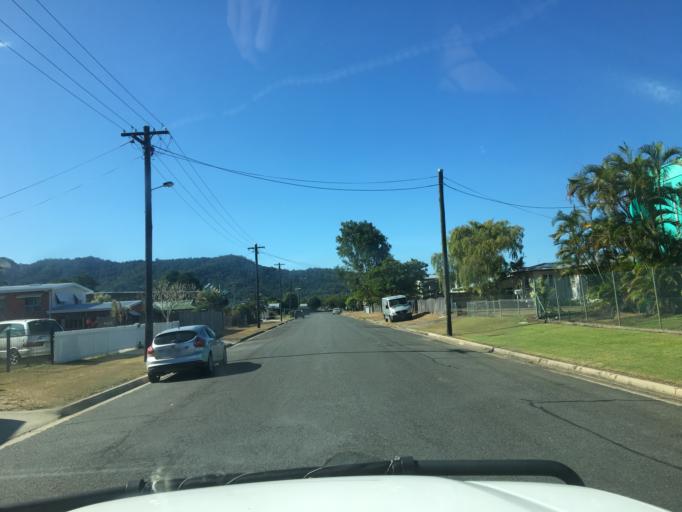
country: AU
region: Queensland
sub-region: Cairns
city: Cairns
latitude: -16.9137
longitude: 145.7464
